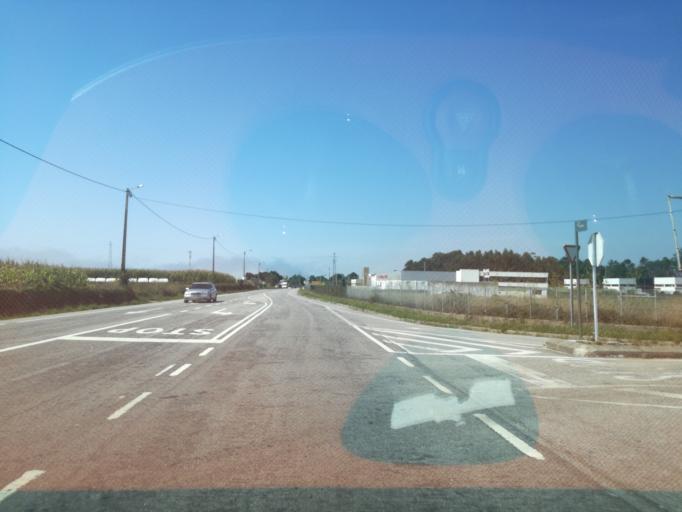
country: PT
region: Braga
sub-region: Esposende
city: Apulia
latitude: 41.4987
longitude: -8.7583
